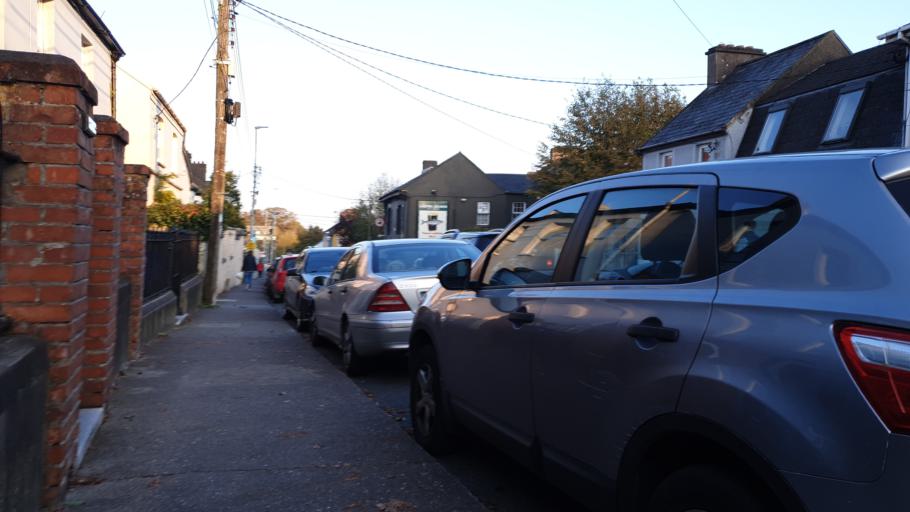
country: IE
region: Munster
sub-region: County Cork
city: Cork
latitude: 51.8971
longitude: -8.4163
